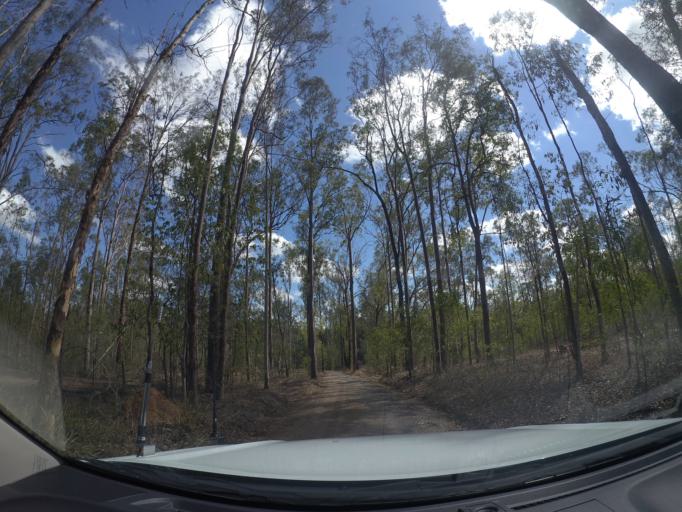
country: AU
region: Queensland
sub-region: Logan
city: Cedar Vale
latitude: -27.8345
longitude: 152.9668
